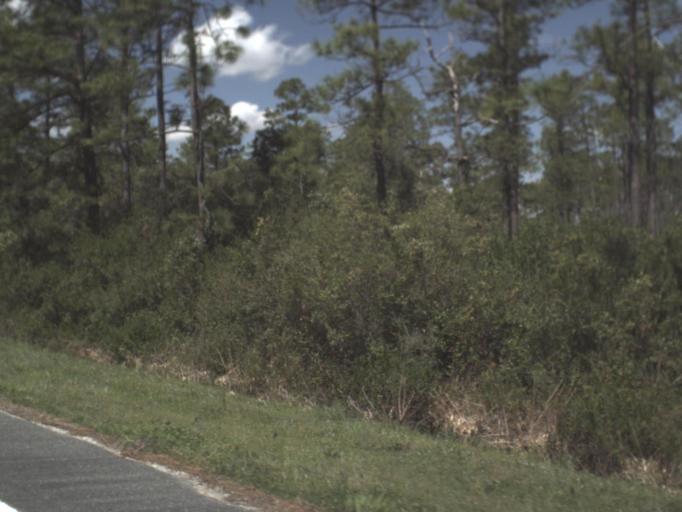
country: US
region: Florida
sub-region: Gadsden County
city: Midway
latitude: 30.3400
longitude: -84.4900
